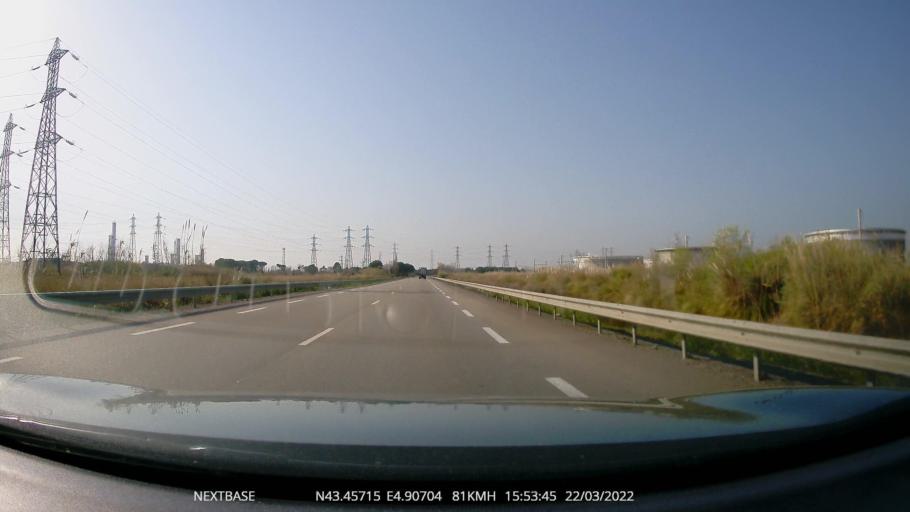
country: FR
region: Provence-Alpes-Cote d'Azur
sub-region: Departement des Bouches-du-Rhone
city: Fos-sur-Mer
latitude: 43.4573
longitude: 4.9072
